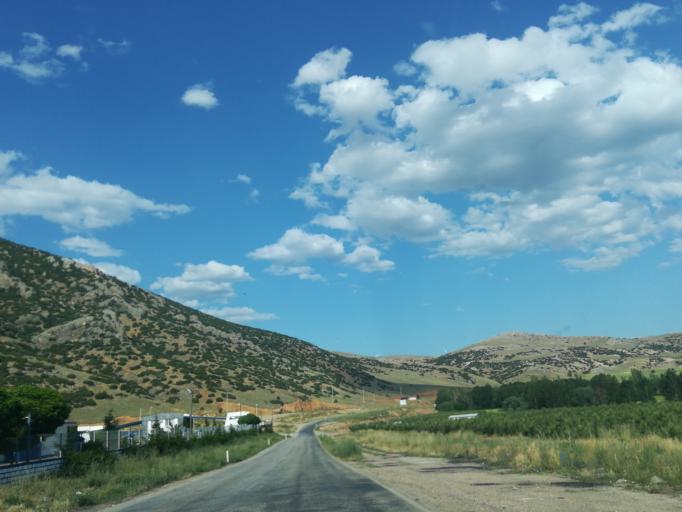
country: TR
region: Afyonkarahisar
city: Dinar
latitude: 38.0990
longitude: 30.1477
